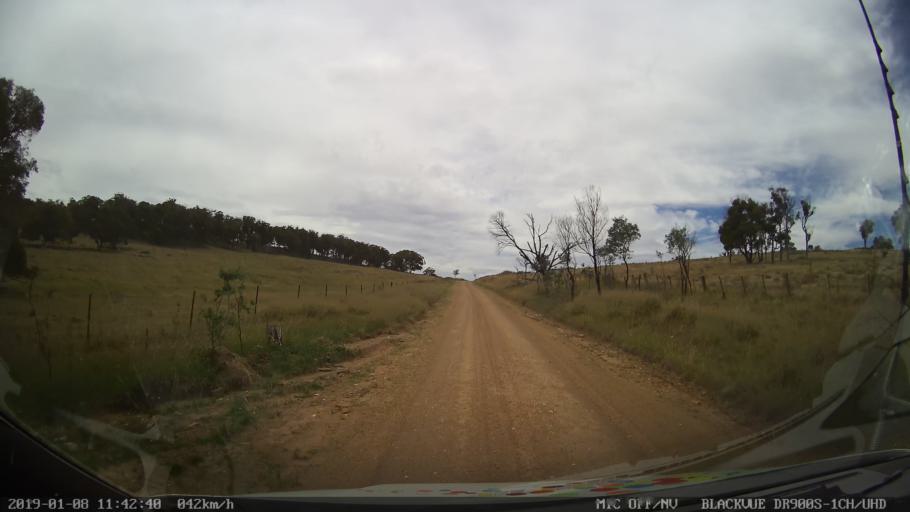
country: AU
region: New South Wales
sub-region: Armidale Dumaresq
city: Armidale
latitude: -30.3791
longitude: 151.5772
